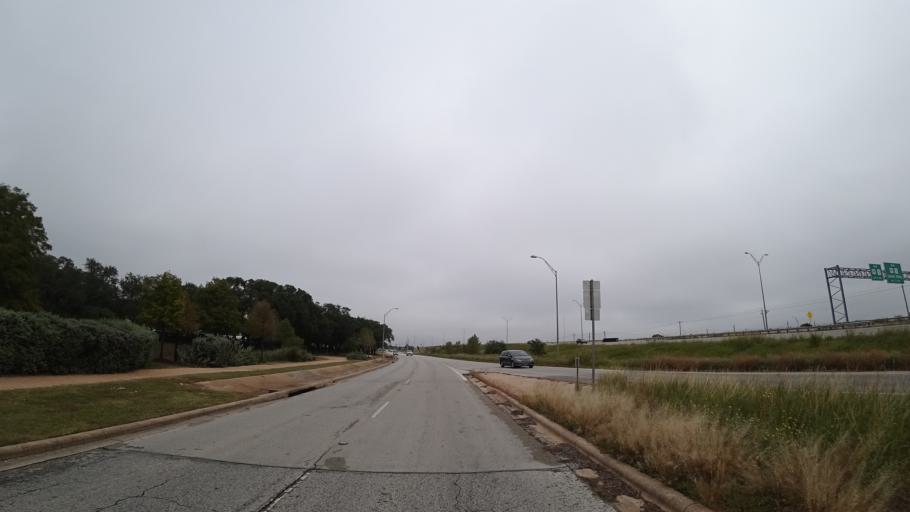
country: US
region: Texas
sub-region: Travis County
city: Shady Hollow
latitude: 30.2188
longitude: -97.8385
